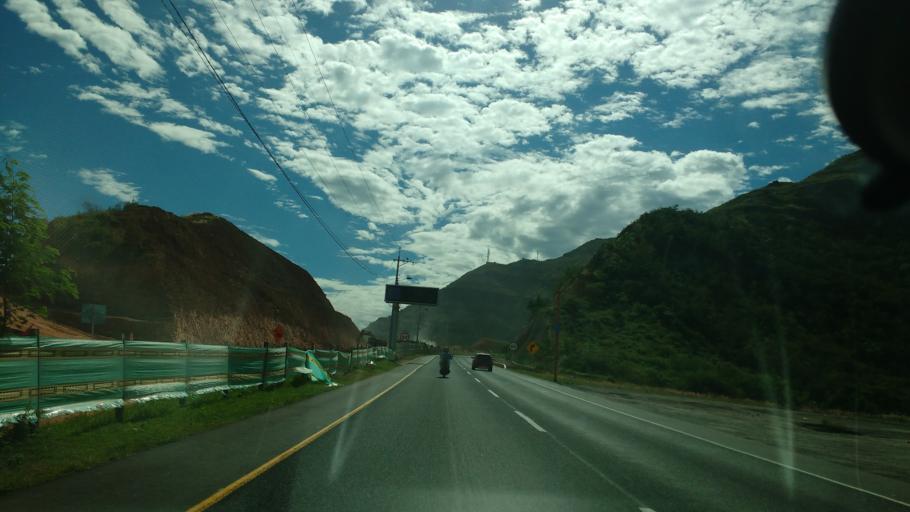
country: CO
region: Tolima
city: Valle de San Juan
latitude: 4.2813
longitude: -75.0170
